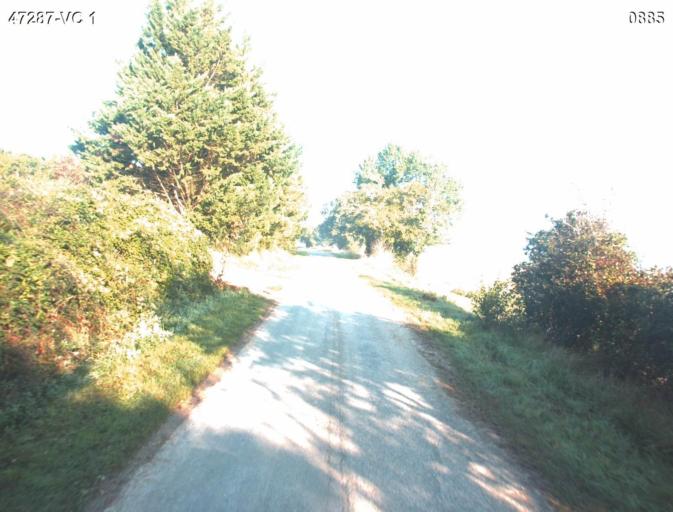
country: FR
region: Aquitaine
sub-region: Departement du Lot-et-Garonne
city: Laplume
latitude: 44.1306
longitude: 0.4538
